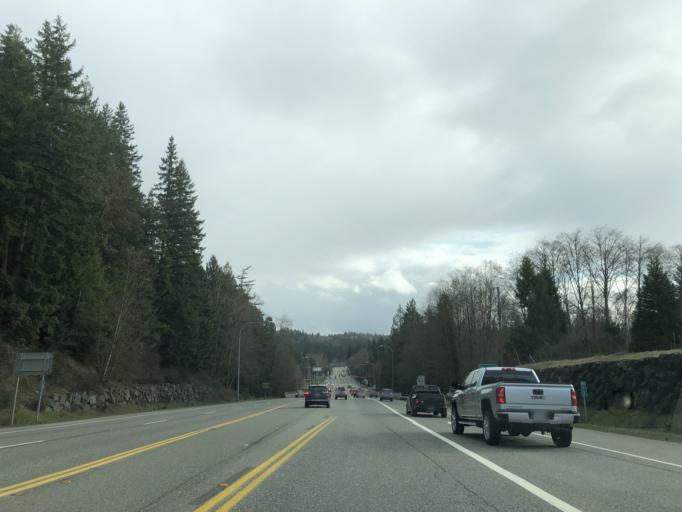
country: US
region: Washington
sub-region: Kitsap County
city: Poulsbo
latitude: 47.7541
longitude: -122.6486
